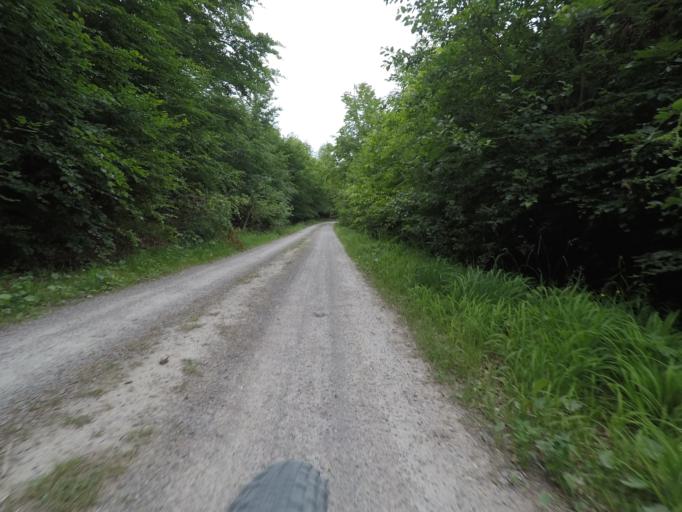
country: DE
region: Baden-Wuerttemberg
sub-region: Regierungsbezirk Stuttgart
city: Hildrizhausen
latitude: 48.5758
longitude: 8.9727
